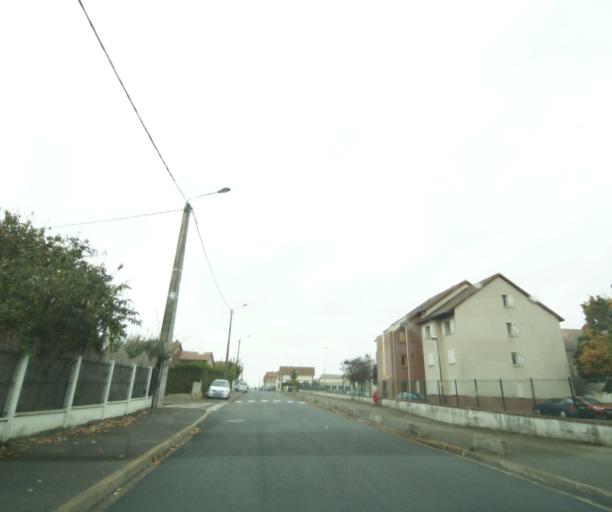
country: FR
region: Centre
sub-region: Departement d'Eure-et-Loir
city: Dreux
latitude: 48.7418
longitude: 1.3586
